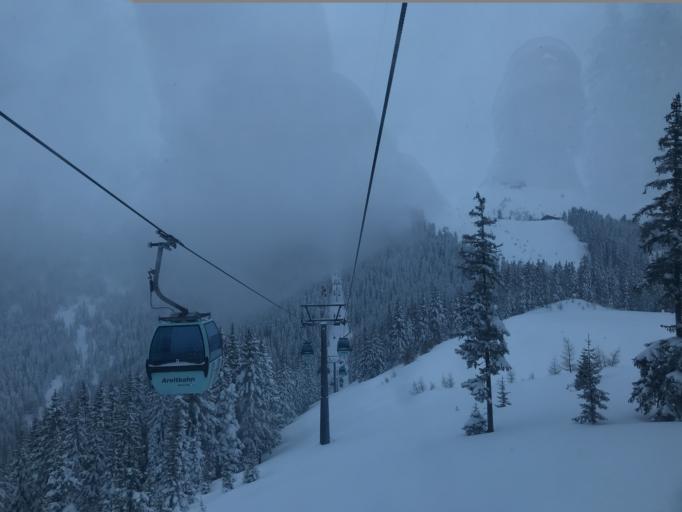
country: AT
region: Salzburg
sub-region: Politischer Bezirk Zell am See
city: Kaprun
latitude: 47.3161
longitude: 12.7493
